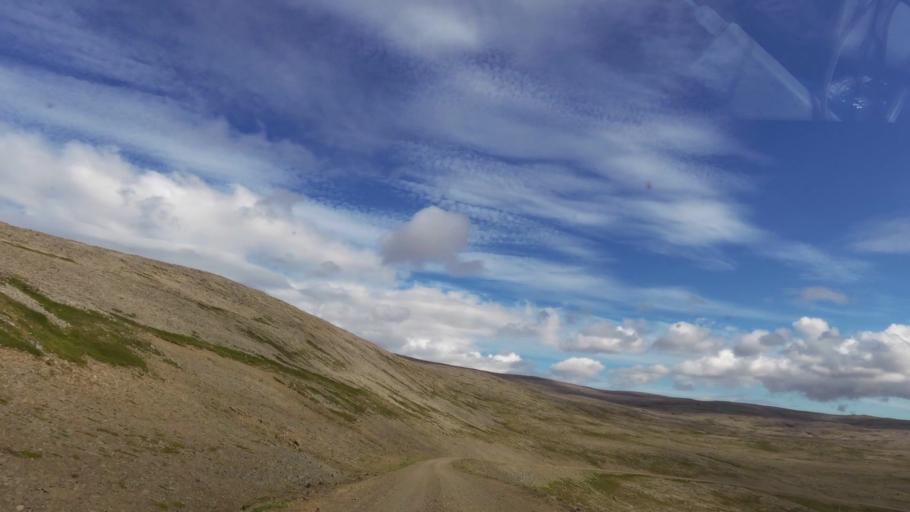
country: IS
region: West
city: Olafsvik
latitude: 65.6176
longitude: -24.3097
